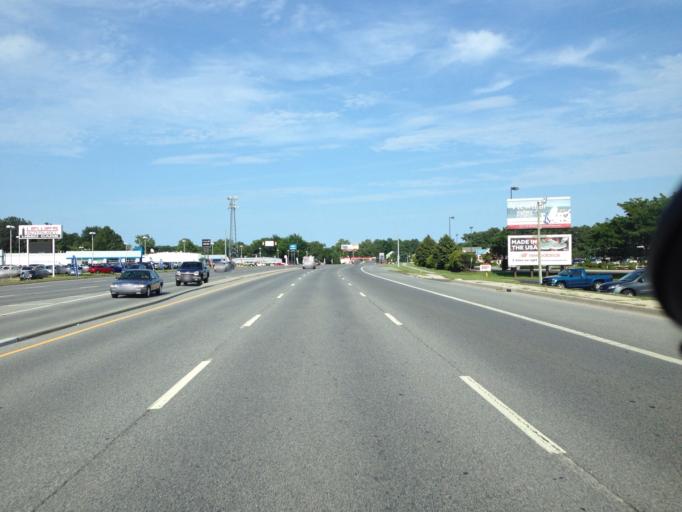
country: US
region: Delaware
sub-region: Sussex County
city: Lewes
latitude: 38.7484
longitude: -75.1648
